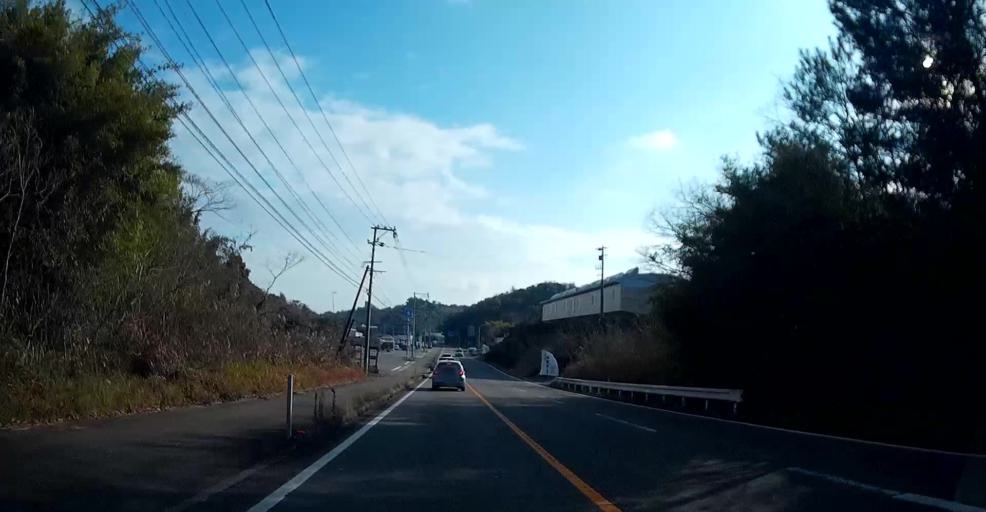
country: JP
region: Kumamoto
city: Yatsushiro
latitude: 32.5560
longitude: 130.4162
